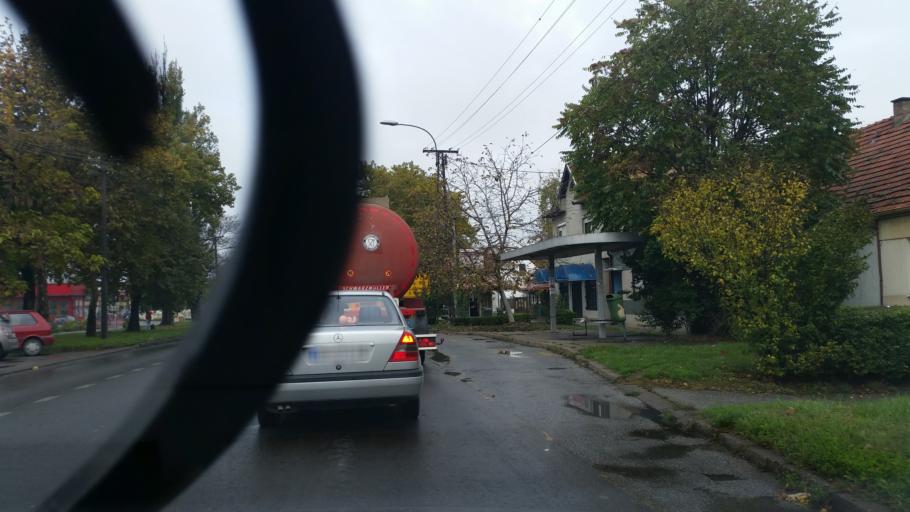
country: RS
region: Autonomna Pokrajina Vojvodina
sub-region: Srednjebanatski Okrug
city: Zrenjanin
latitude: 45.3762
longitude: 20.4093
